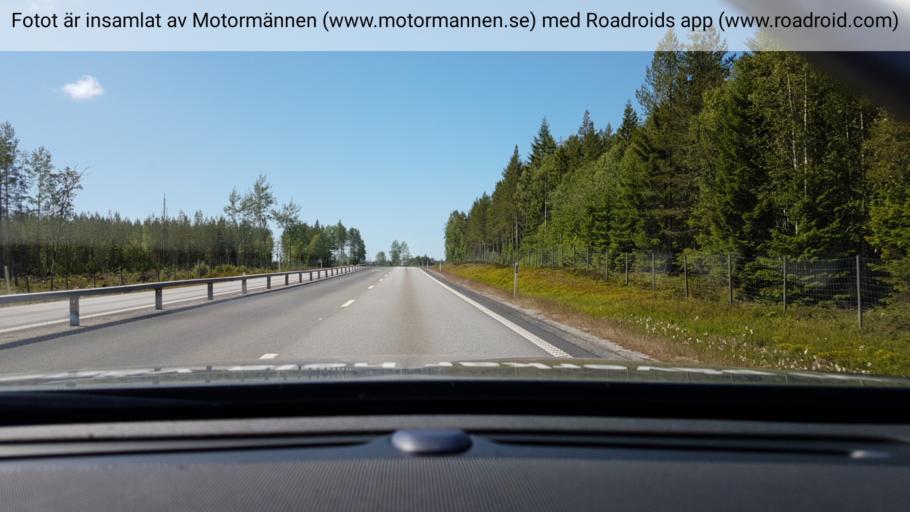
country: SE
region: Vaesterbotten
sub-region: Umea Kommun
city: Hoernefors
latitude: 63.6211
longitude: 19.8412
